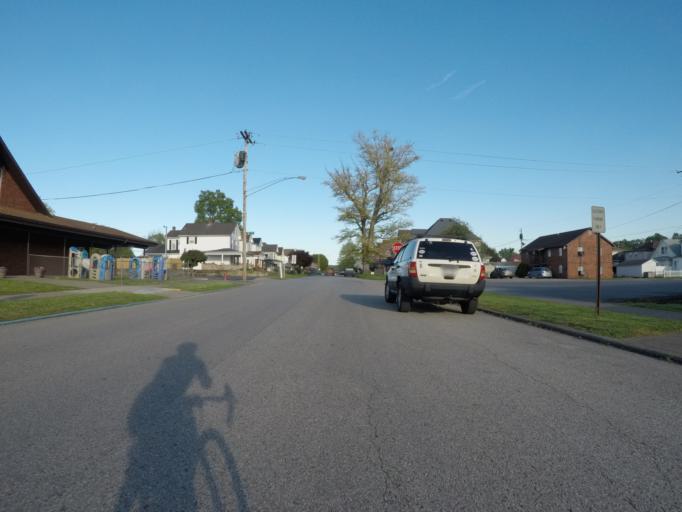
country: US
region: West Virginia
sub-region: Wayne County
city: Kenova
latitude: 38.4011
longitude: -82.5840
